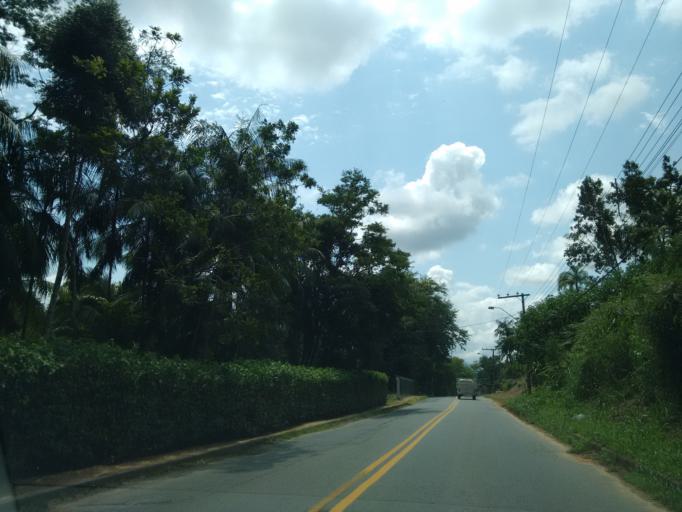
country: BR
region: Santa Catarina
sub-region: Blumenau
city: Blumenau
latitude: -26.8661
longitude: -49.1416
